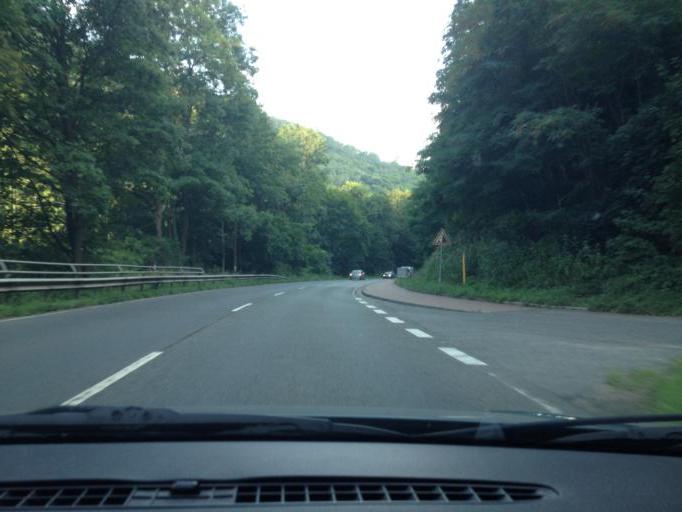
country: DE
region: Rheinland-Pfalz
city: Lindenberg
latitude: 49.3663
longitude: 8.1069
